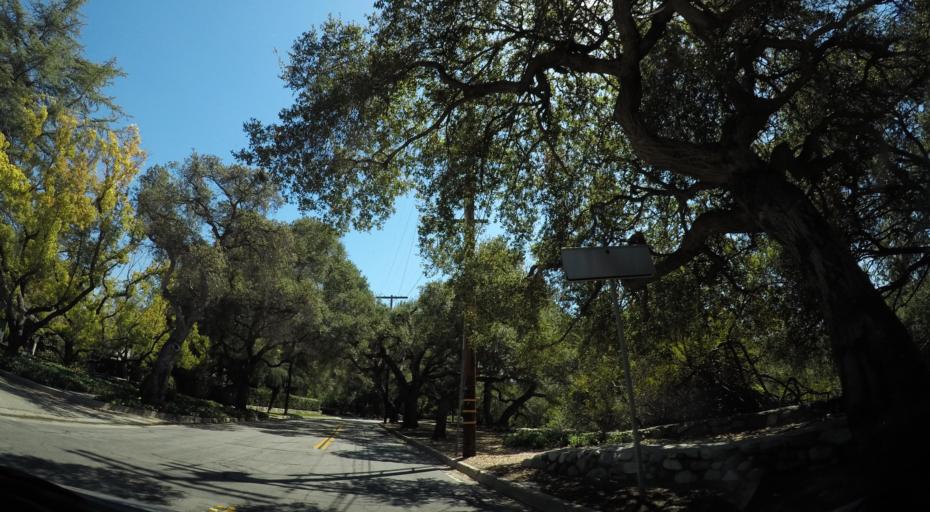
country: US
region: California
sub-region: Los Angeles County
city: Pasadena
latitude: 34.1422
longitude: -118.1661
